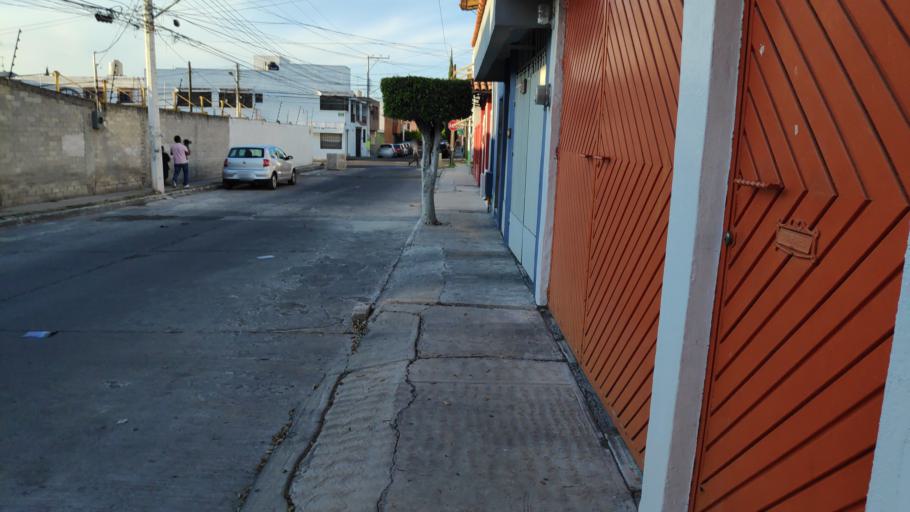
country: MX
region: Queretaro
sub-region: Queretaro
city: Santiago de Queretaro
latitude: 20.5815
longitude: -100.3823
